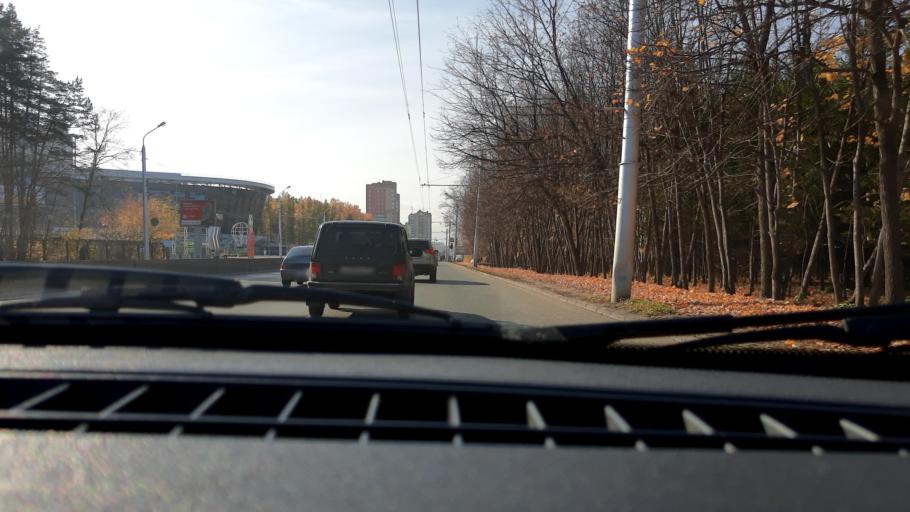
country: RU
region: Bashkortostan
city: Ufa
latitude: 54.7271
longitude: 56.0209
